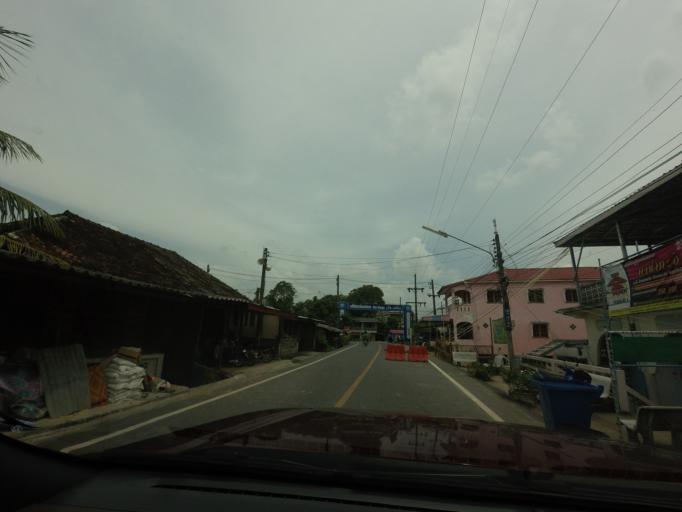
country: TH
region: Pattani
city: Yarang
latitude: 6.7128
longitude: 101.2914
